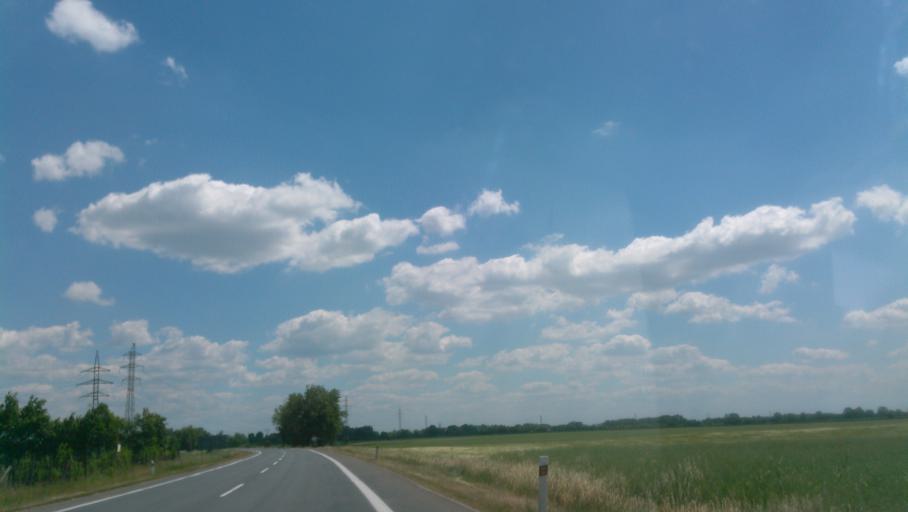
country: SK
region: Trnavsky
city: Dunajska Streda
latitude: 47.9837
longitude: 17.5879
